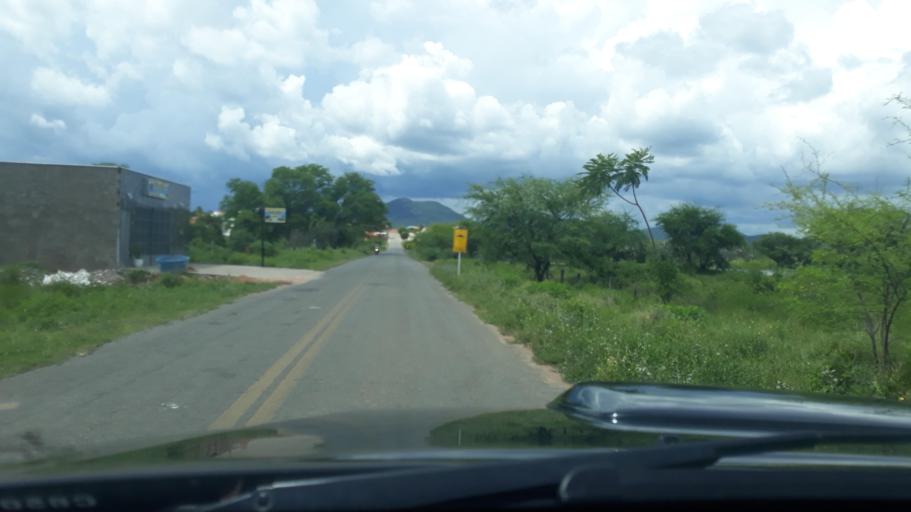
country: BR
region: Bahia
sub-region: Guanambi
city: Guanambi
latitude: -13.9151
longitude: -42.8441
